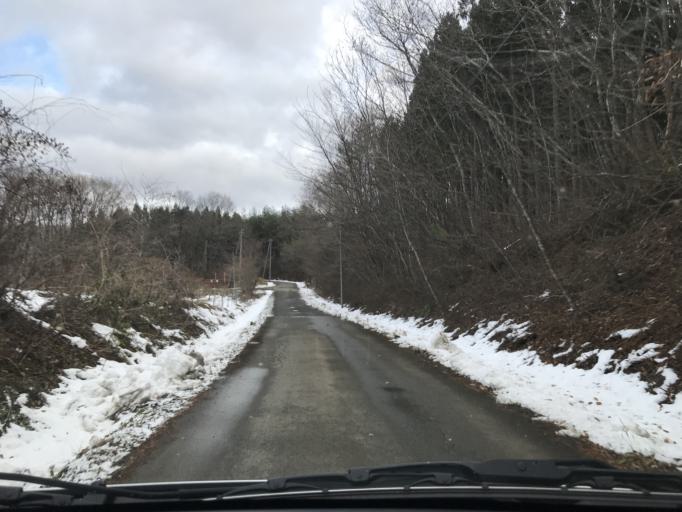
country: JP
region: Iwate
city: Ichinoseki
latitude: 38.9758
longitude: 141.0254
